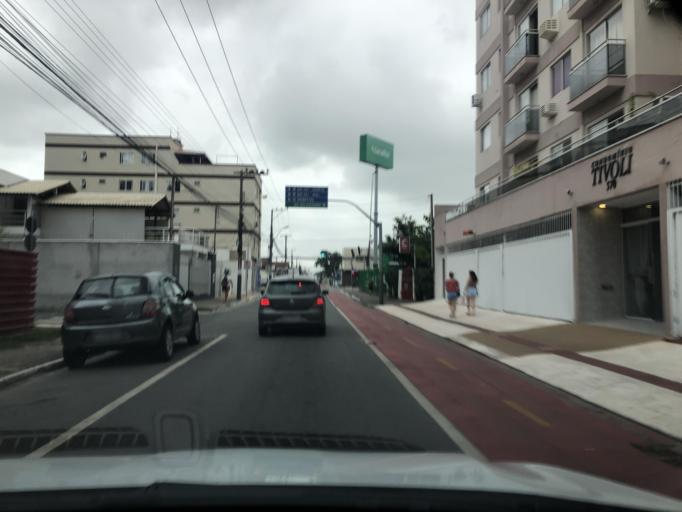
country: BR
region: Santa Catarina
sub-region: Balneario Camboriu
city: Balneario Camboriu
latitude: -26.9999
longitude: -48.6298
